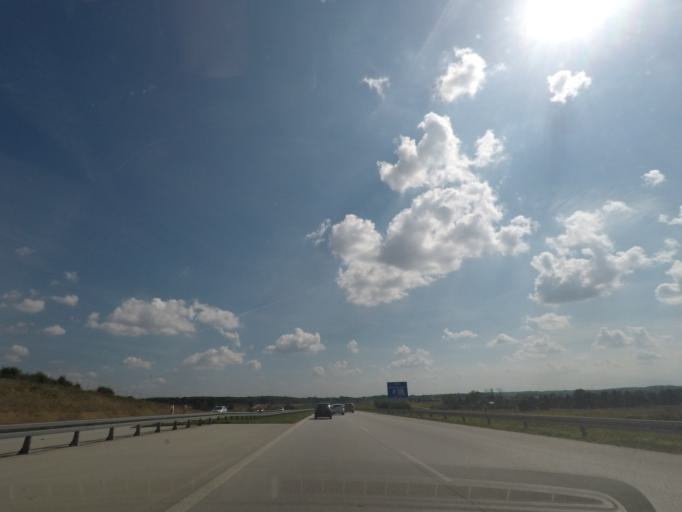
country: PL
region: Lodz Voivodeship
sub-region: Powiat zgierski
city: Strykow
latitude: 51.8512
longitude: 19.6600
